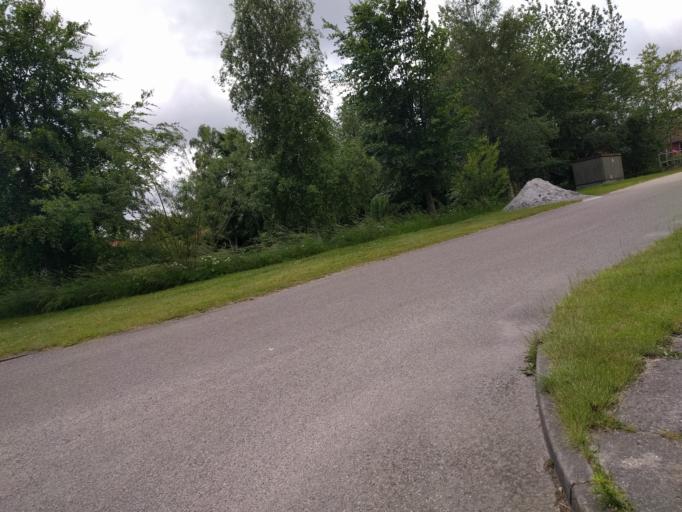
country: DK
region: South Denmark
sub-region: Odense Kommune
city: Bullerup
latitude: 55.4260
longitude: 10.4669
